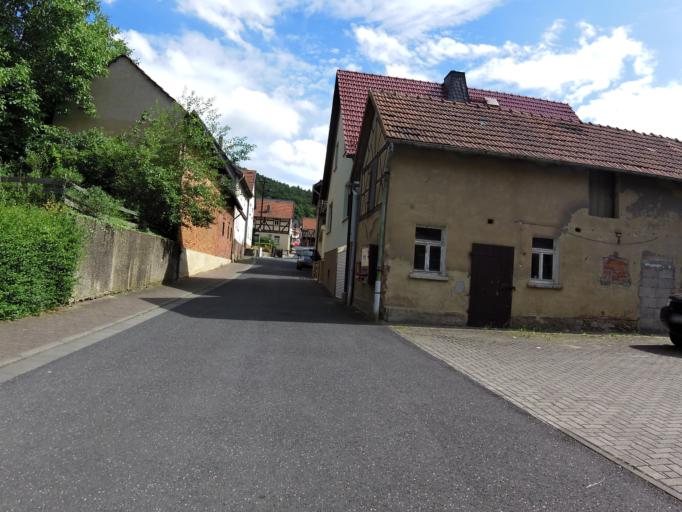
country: DE
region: Thuringia
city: Dorndorf
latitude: 50.8418
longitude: 10.1218
